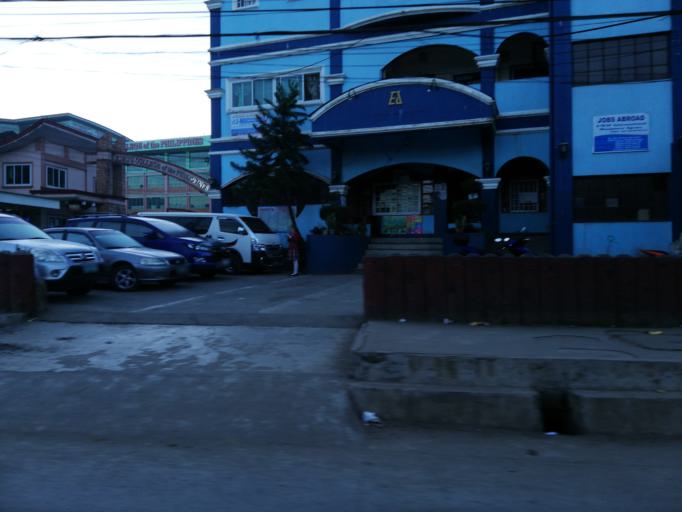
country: PH
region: Cordillera
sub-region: Province of Benguet
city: La Trinidad
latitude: 16.4455
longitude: 120.5871
